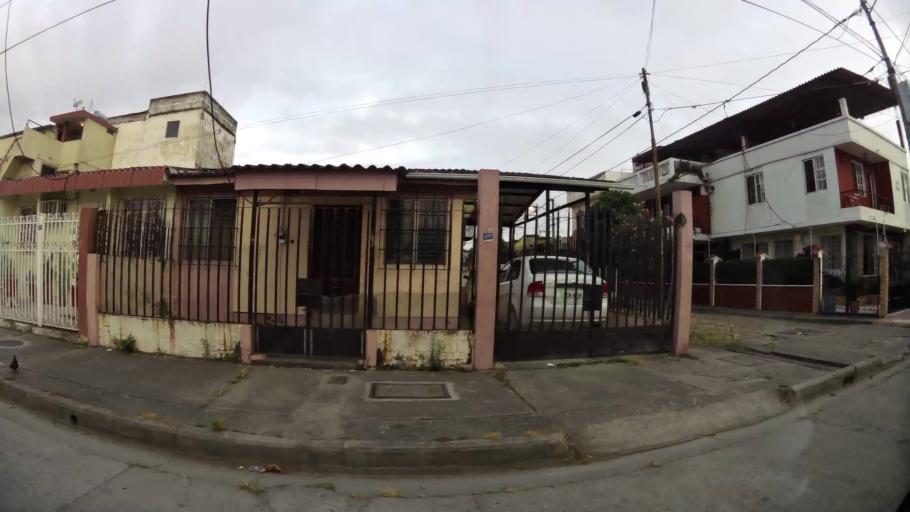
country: EC
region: Guayas
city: Eloy Alfaro
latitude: -2.1748
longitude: -79.8855
